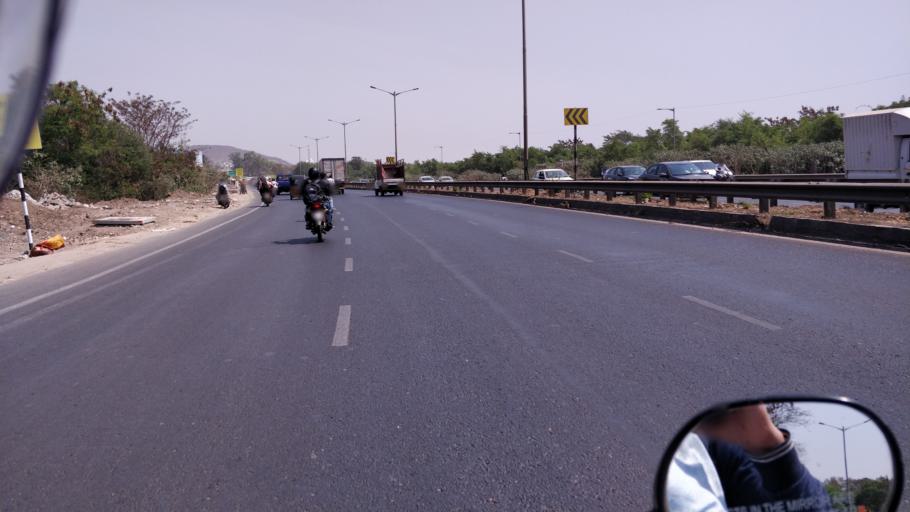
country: IN
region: Maharashtra
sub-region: Pune Division
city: Shivaji Nagar
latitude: 18.5291
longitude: 73.7783
